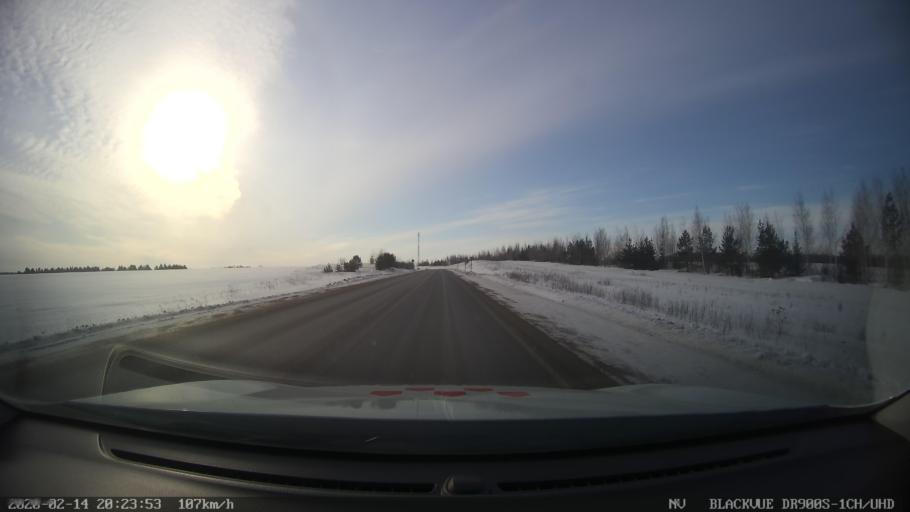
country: RU
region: Tatarstan
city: Verkhniy Uslon
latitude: 55.5216
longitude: 48.9689
